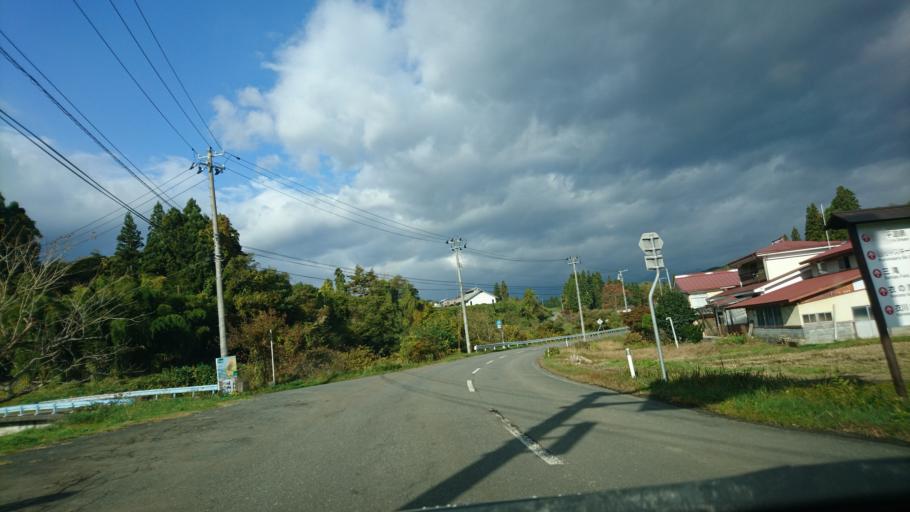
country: JP
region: Iwate
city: Mizusawa
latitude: 39.0782
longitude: 141.0024
